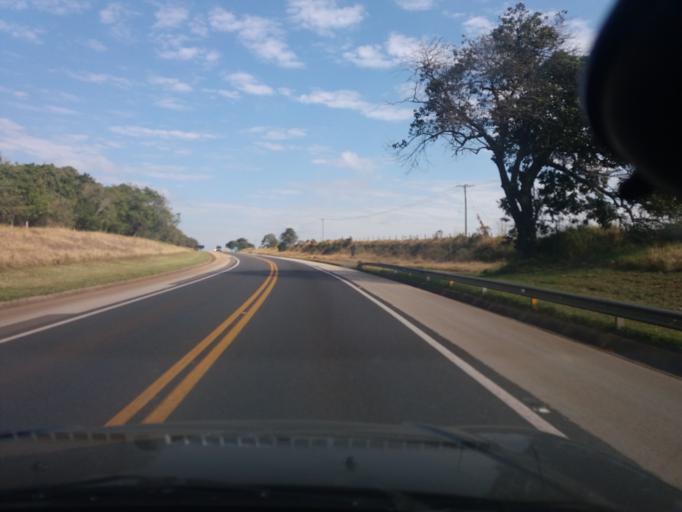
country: BR
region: Sao Paulo
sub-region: Buri
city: Buri
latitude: -23.9373
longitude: -48.6038
